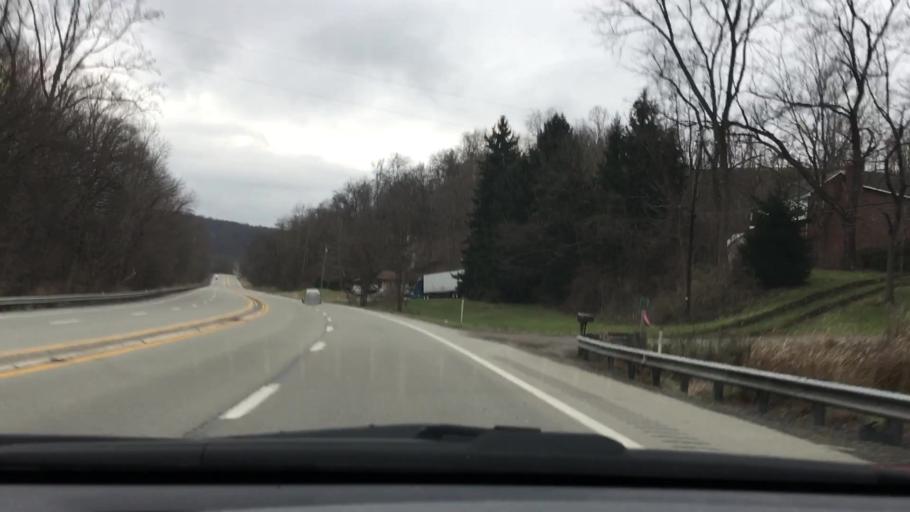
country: US
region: Pennsylvania
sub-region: Fayette County
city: Perryopolis
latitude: 40.0128
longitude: -79.7660
